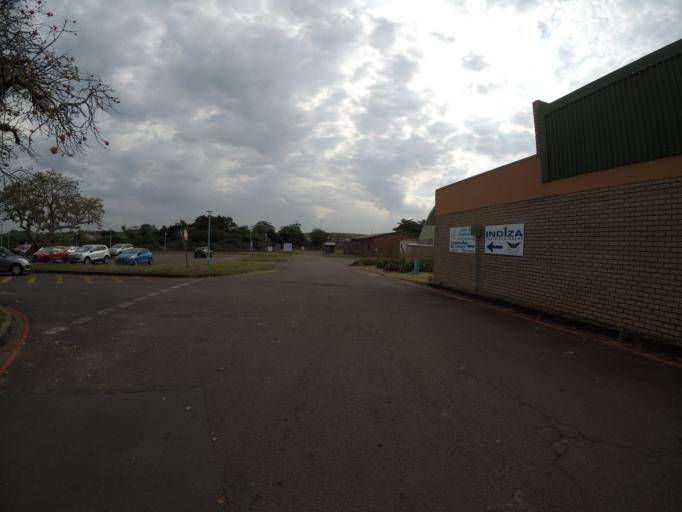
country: ZA
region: KwaZulu-Natal
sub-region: uThungulu District Municipality
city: Richards Bay
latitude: -28.7366
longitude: 32.0938
